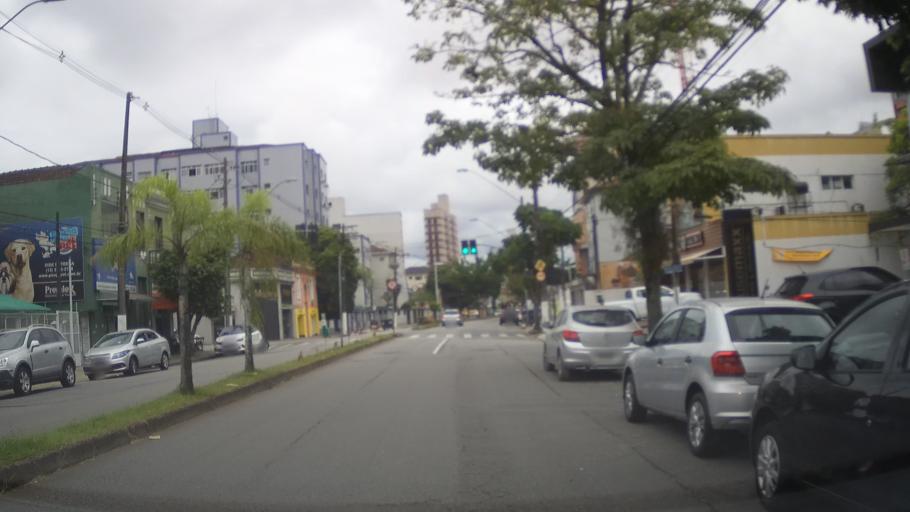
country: BR
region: Sao Paulo
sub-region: Santos
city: Santos
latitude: -23.9671
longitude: -46.3150
